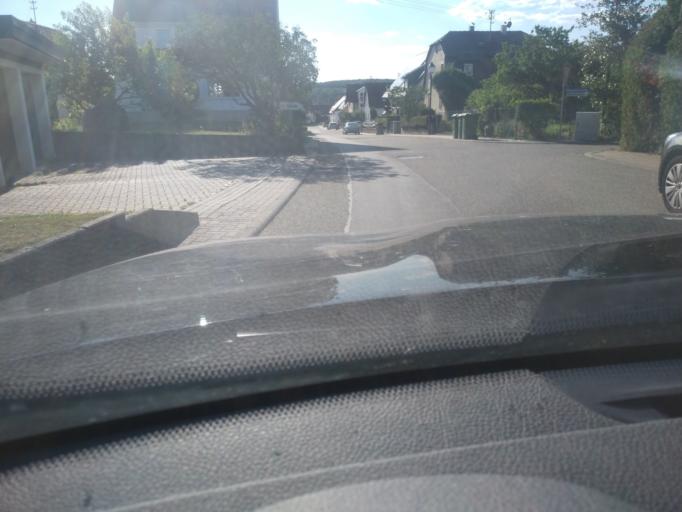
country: DE
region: Baden-Wuerttemberg
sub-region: Karlsruhe Region
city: Wurmberg
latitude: 48.8808
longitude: 8.7997
